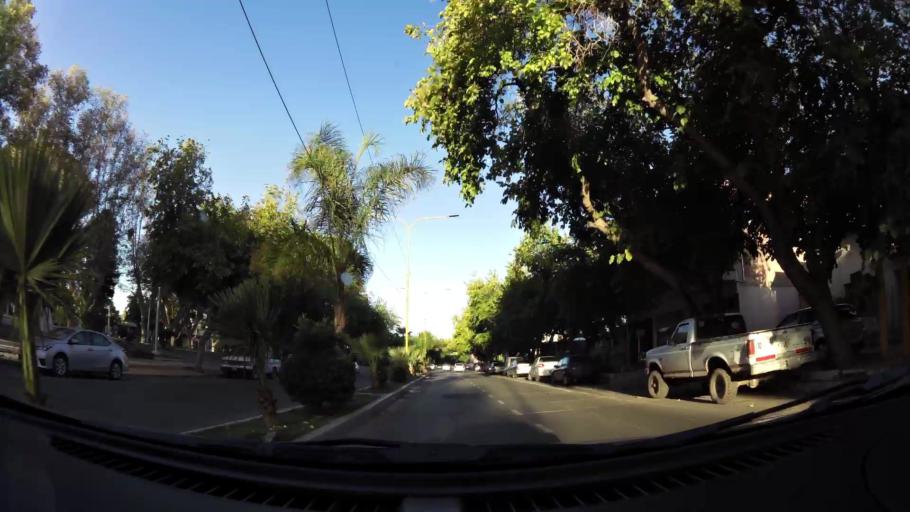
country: AR
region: San Juan
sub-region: Departamento de Santa Lucia
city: Santa Lucia
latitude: -31.5412
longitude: -68.4980
